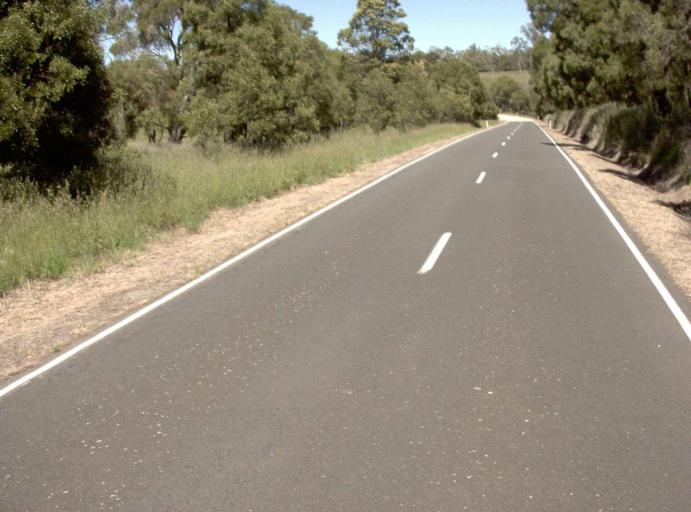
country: AU
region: Victoria
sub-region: East Gippsland
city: Lakes Entrance
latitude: -37.2496
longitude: 148.2520
